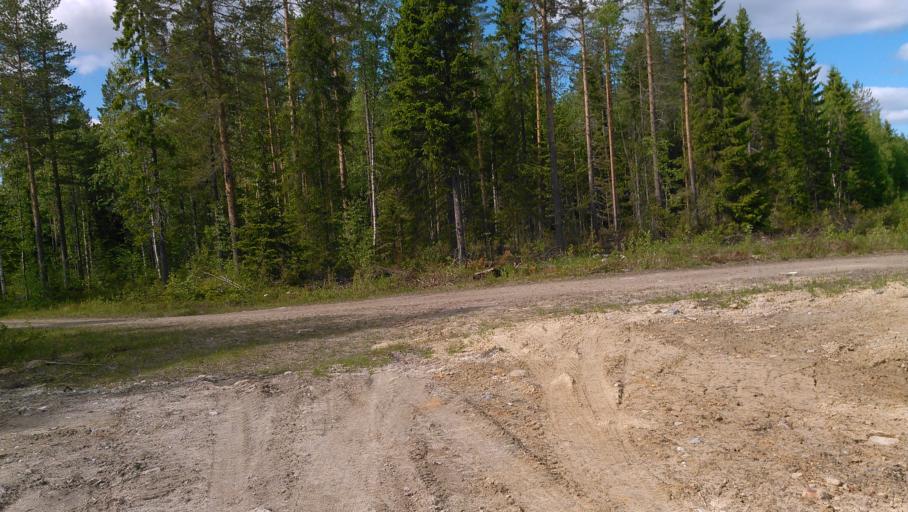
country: SE
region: Vaesterbotten
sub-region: Vannas Kommun
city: Vannasby
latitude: 63.9161
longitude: 19.9353
